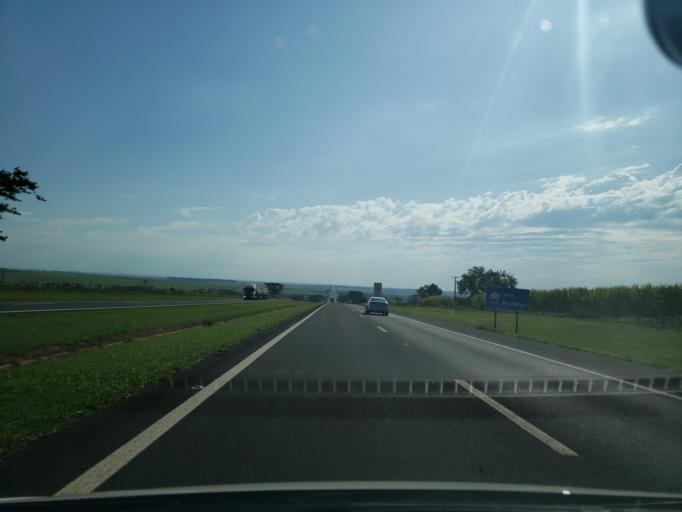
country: BR
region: Sao Paulo
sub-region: Penapolis
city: Penapolis
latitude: -21.5081
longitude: -50.0218
